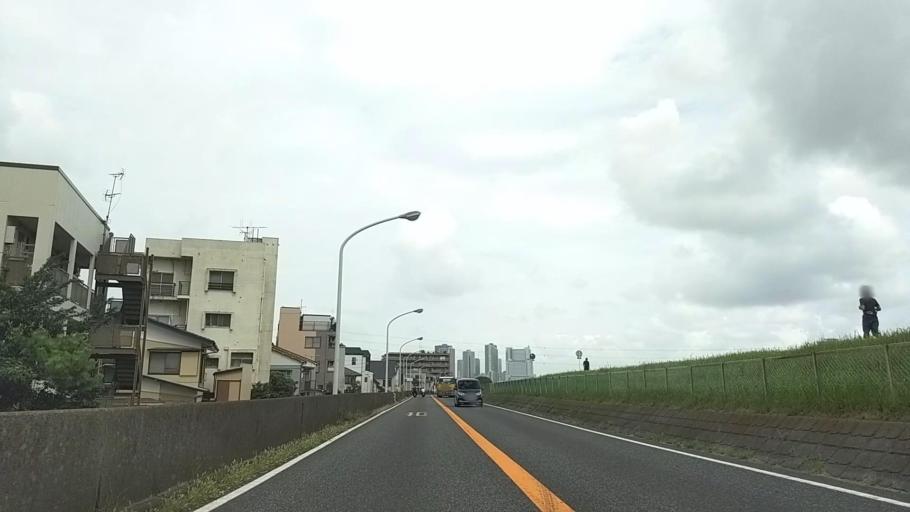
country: JP
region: Kanagawa
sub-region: Kawasaki-shi
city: Kawasaki
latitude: 35.5563
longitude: 139.6851
